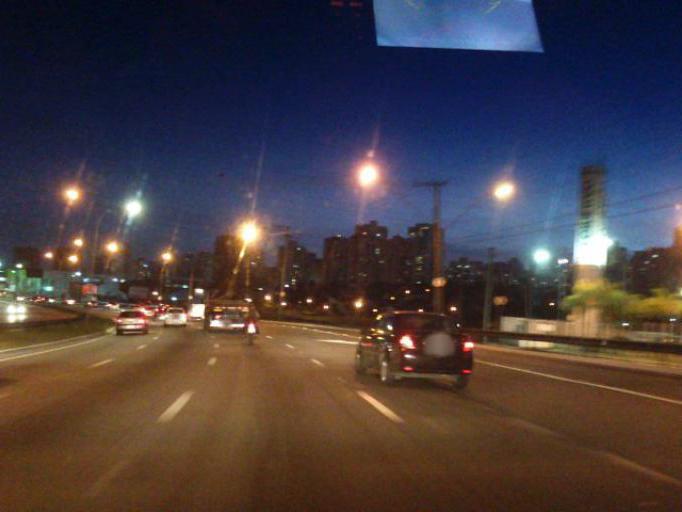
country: BR
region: Sao Paulo
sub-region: Sao Jose Dos Campos
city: Sao Jose dos Campos
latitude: -23.2124
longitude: -45.9005
